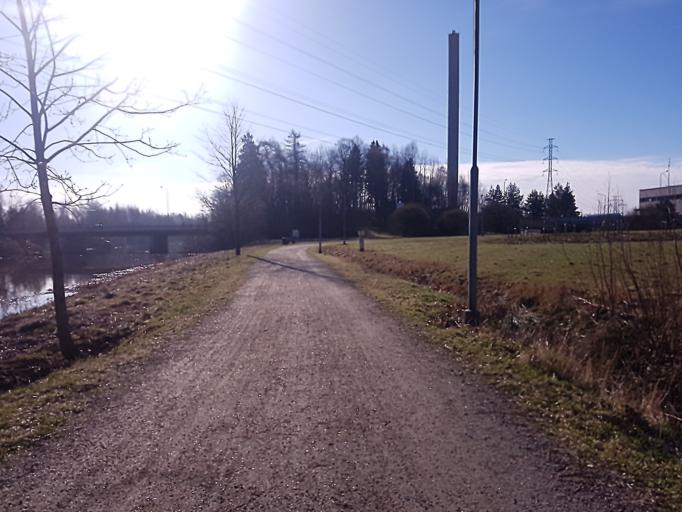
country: FI
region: Uusimaa
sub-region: Helsinki
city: Helsinki
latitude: 60.2395
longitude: 24.9759
